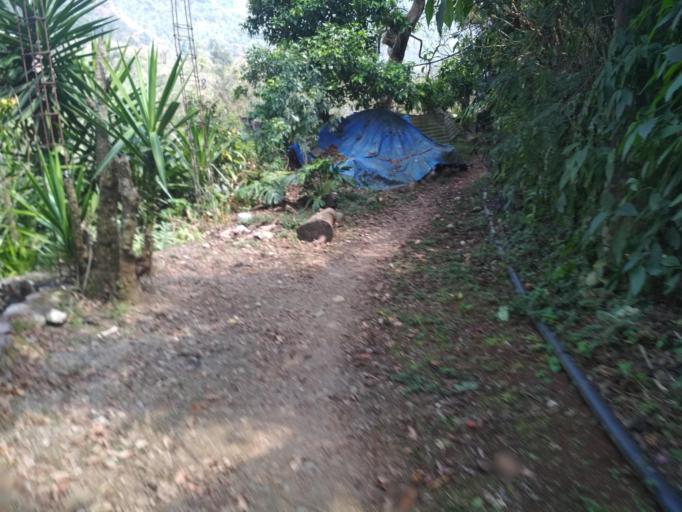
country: MX
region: Veracruz
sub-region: Tlilapan
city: Tonalixco
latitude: 18.7848
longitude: -97.0866
